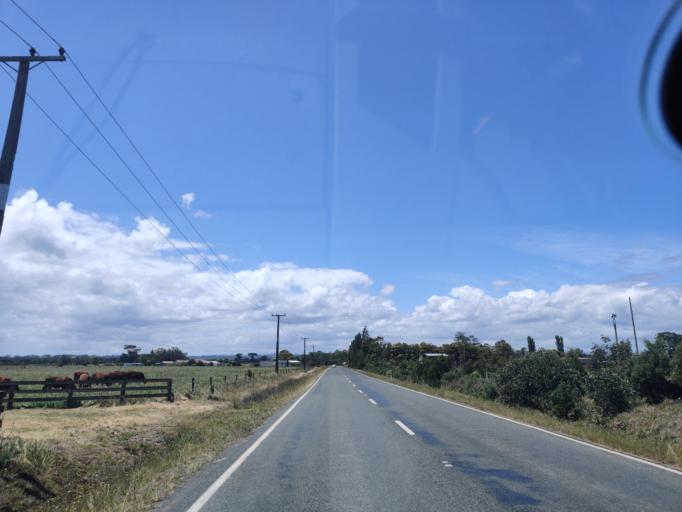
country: NZ
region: Northland
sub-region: Far North District
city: Kaitaia
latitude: -35.0235
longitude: 173.2236
